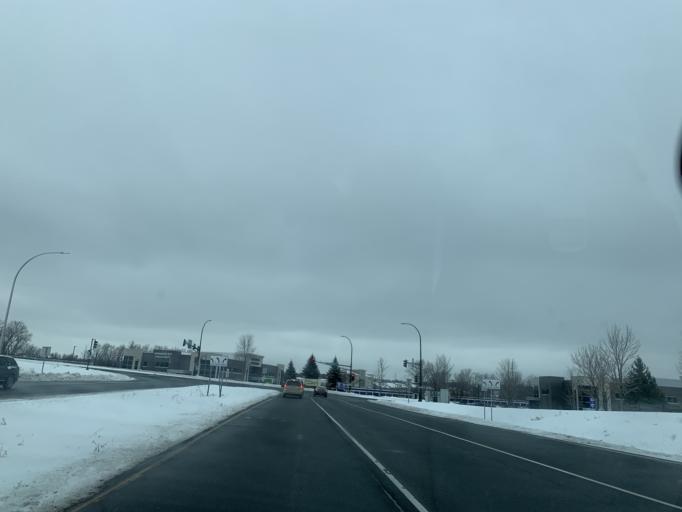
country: US
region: Minnesota
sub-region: Washington County
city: Woodbury
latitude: 44.9374
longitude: -92.9624
